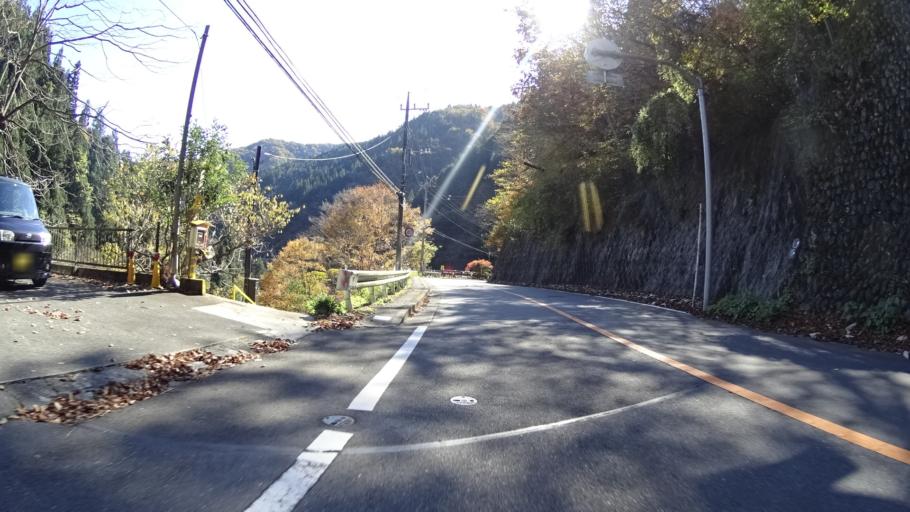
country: JP
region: Yamanashi
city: Uenohara
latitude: 35.7229
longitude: 139.0643
